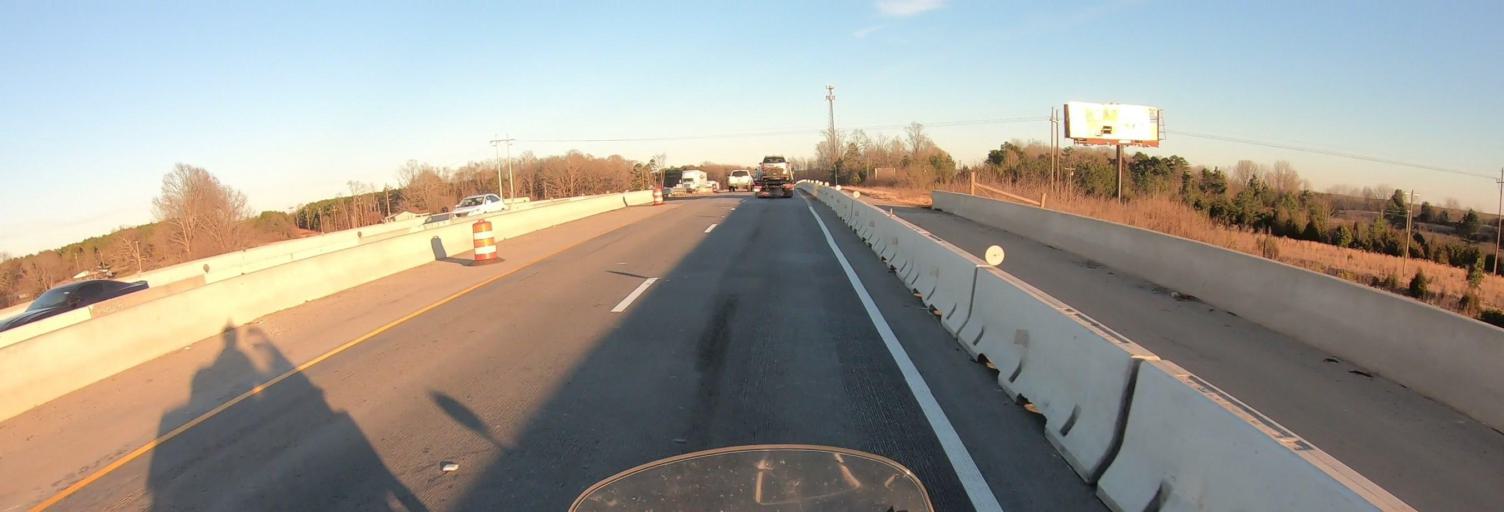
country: US
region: South Carolina
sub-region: Cherokee County
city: Blacksburg
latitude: 35.1587
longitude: -81.4675
